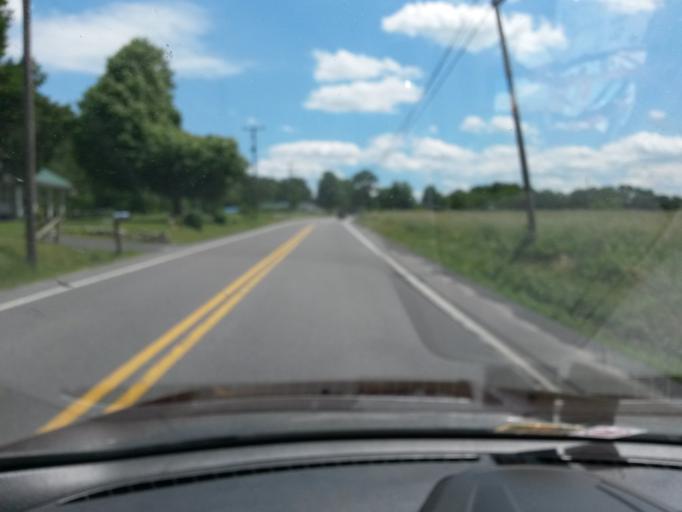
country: US
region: West Virginia
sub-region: Greenbrier County
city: Rainelle
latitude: 37.9278
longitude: -80.6495
